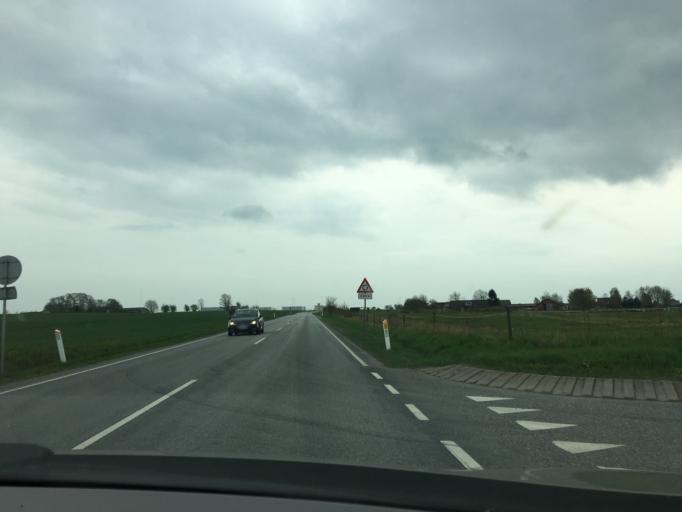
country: DK
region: Central Jutland
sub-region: Horsens Kommune
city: Braedstrup
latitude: 55.8572
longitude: 9.6007
